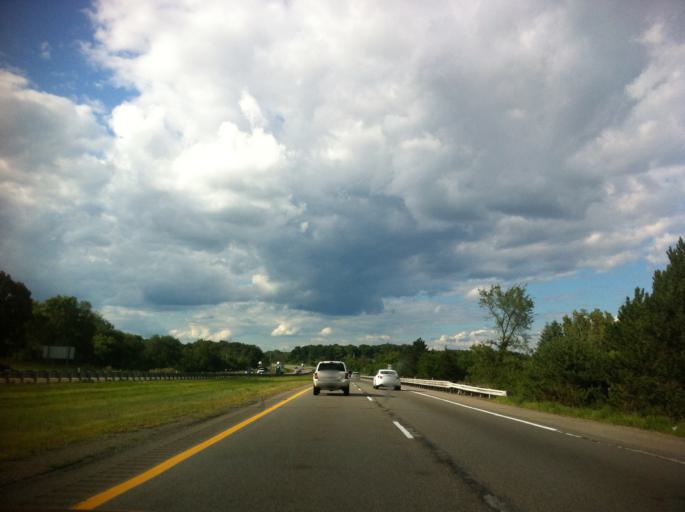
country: US
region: Michigan
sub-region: Livingston County
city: Whitmore Lake
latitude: 42.4484
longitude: -83.7523
